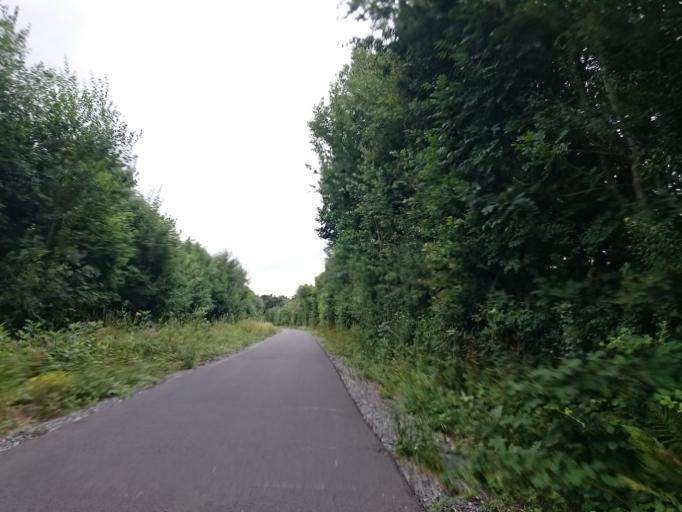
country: FR
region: Lower Normandy
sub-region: Departement du Calvados
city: Bully
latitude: 49.0973
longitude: -0.4039
